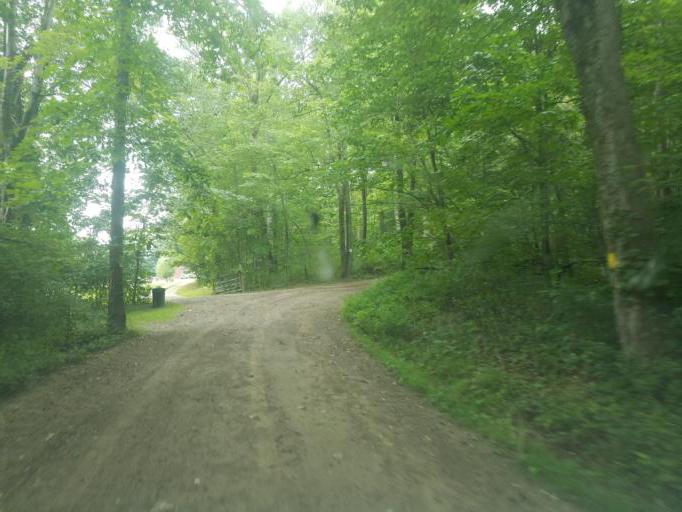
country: US
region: Ohio
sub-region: Ashland County
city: Loudonville
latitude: 40.5729
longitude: -82.3017
